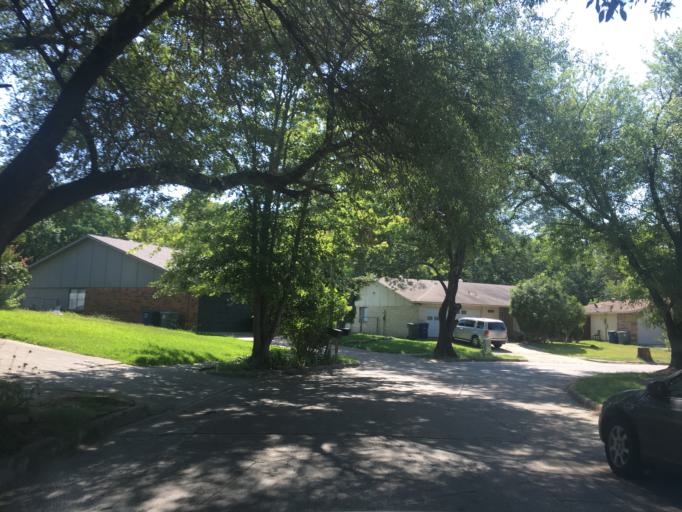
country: US
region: Texas
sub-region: Dallas County
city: Garland
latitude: 32.8555
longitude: -96.6544
